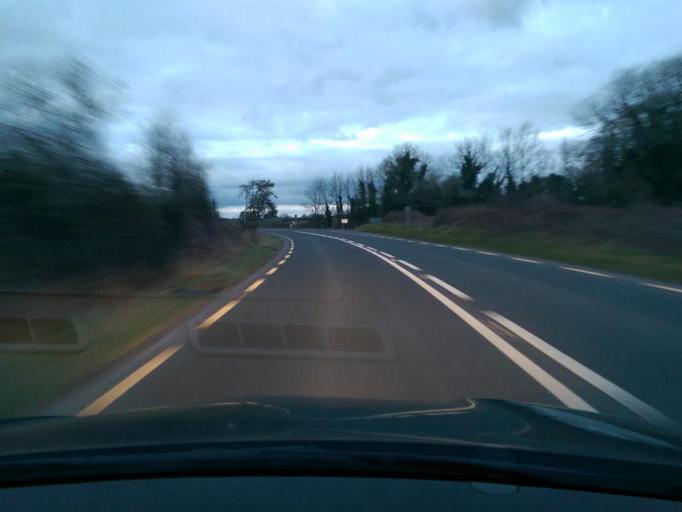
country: IE
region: Connaught
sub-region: County Galway
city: Portumna
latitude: 53.1304
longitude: -8.2462
